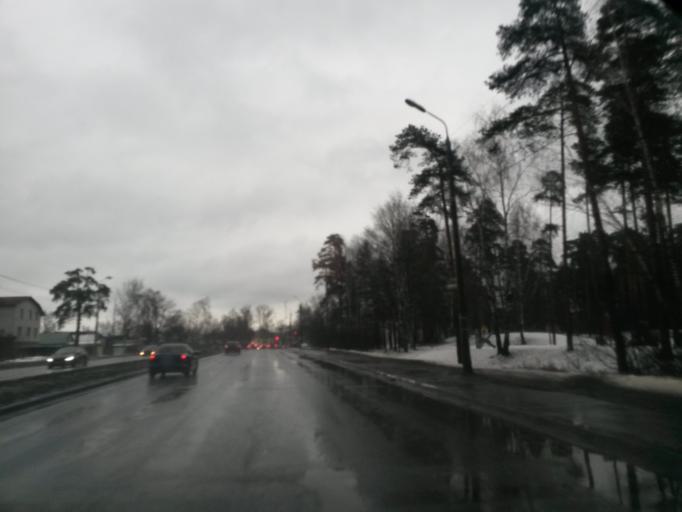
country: RU
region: Jaroslavl
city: Yaroslavl
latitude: 57.6506
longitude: 39.9308
